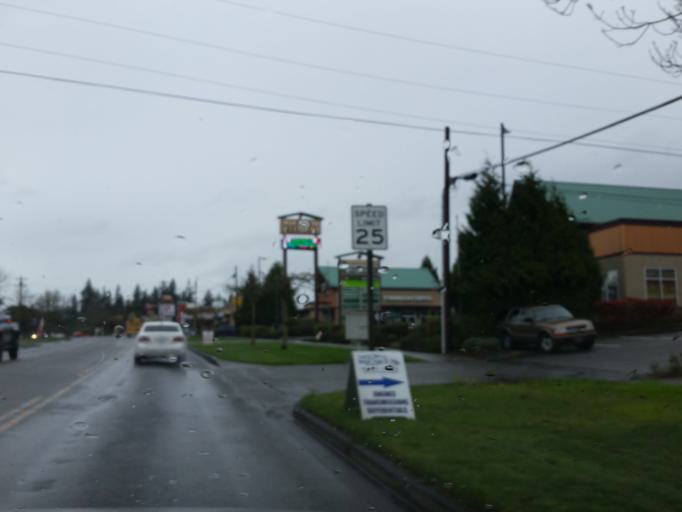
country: US
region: Washington
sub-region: Snohomish County
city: Snohomish
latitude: 47.9246
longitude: -122.0978
